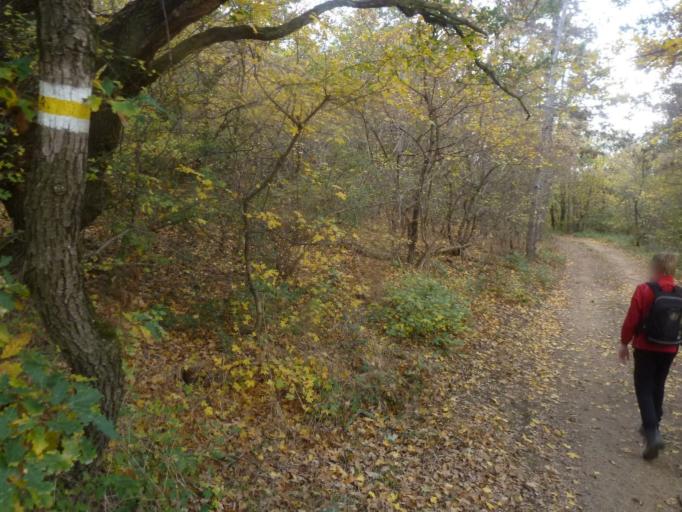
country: HU
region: Fejer
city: Pakozd
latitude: 47.2278
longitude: 18.5470
